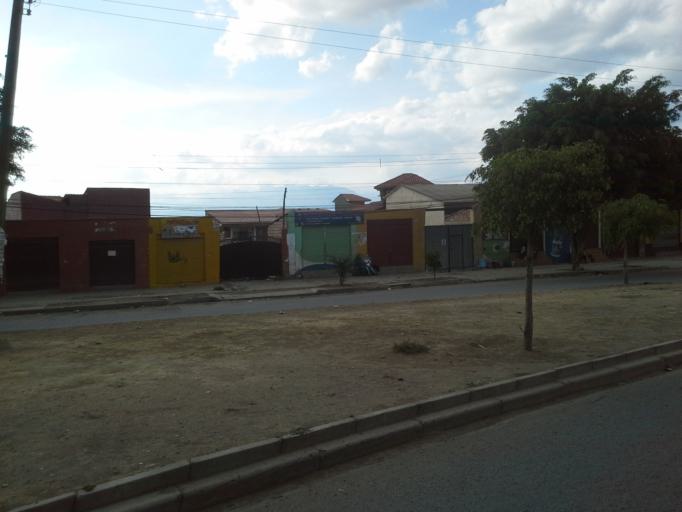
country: BO
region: Cochabamba
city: Cochabamba
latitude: -17.4212
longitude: -66.1531
